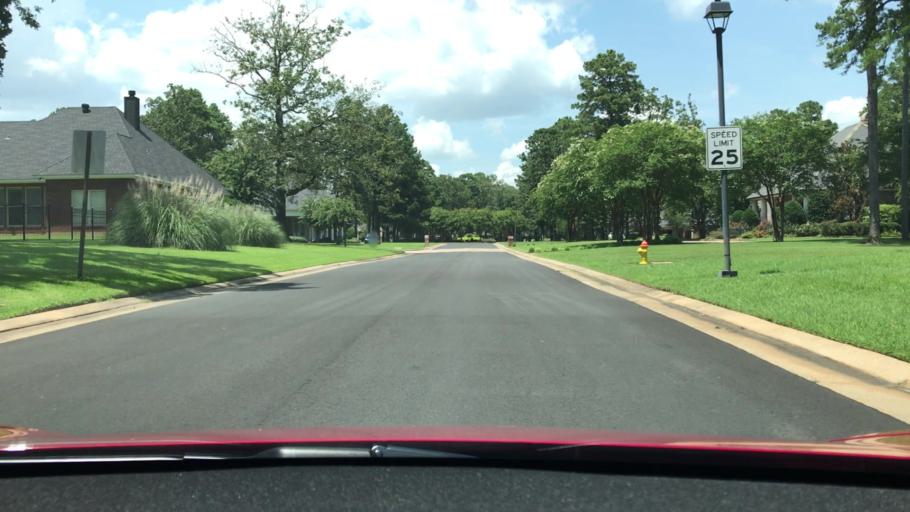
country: US
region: Louisiana
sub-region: De Soto Parish
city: Stonewall
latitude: 32.3605
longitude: -93.7019
